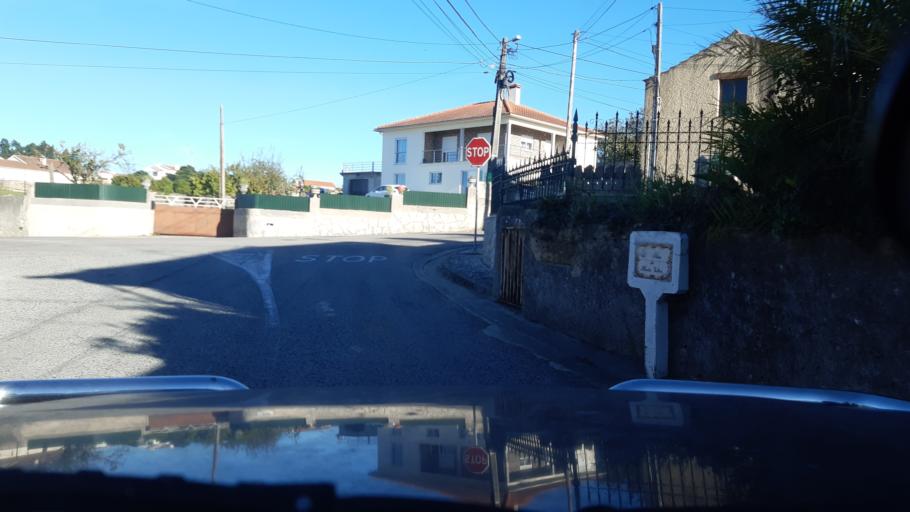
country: PT
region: Aveiro
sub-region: Agueda
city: Agueda
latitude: 40.5560
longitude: -8.4374
